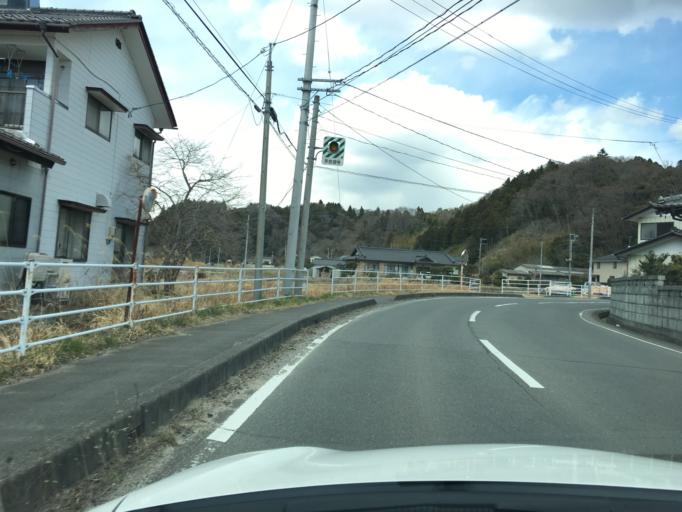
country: JP
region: Fukushima
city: Iwaki
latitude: 37.0625
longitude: 140.9110
